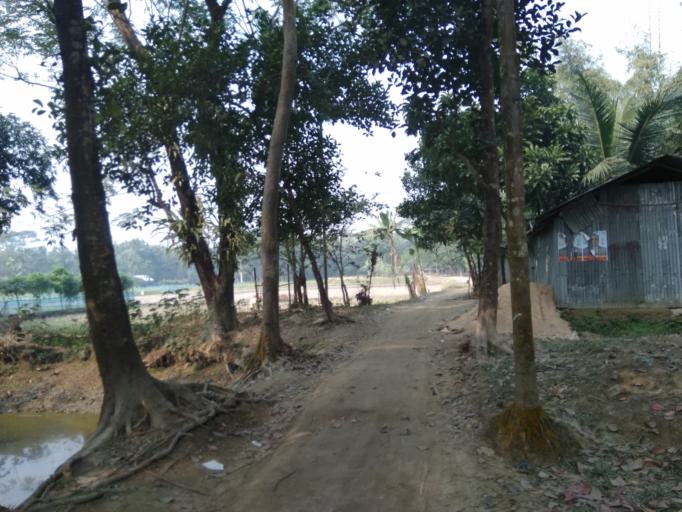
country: BD
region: Dhaka
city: Netrakona
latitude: 24.8924
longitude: 90.6649
